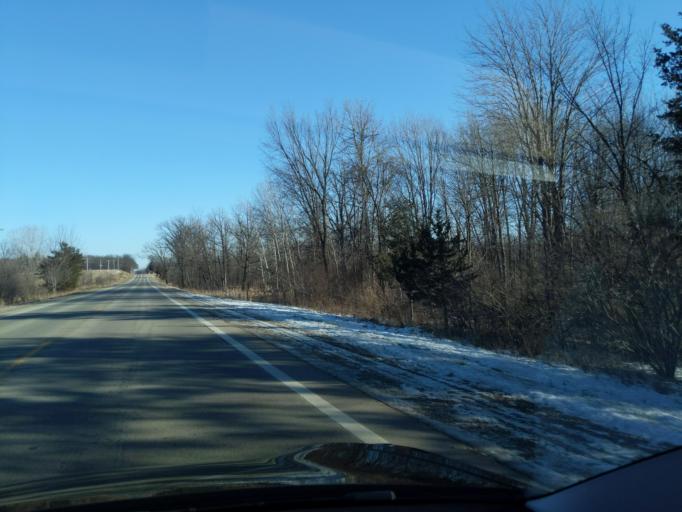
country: US
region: Michigan
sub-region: Ingham County
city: Stockbridge
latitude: 42.3945
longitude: -84.3040
